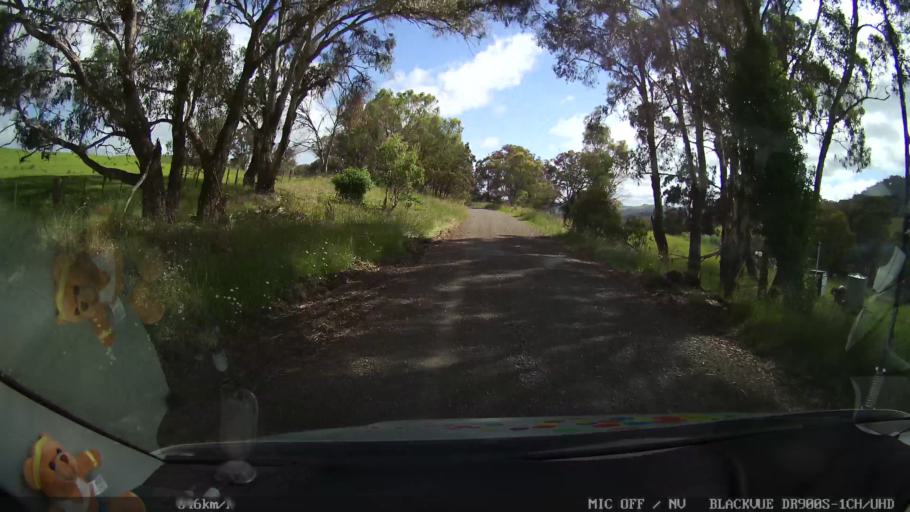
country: AU
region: New South Wales
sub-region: Guyra
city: Guyra
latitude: -30.0048
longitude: 151.6685
